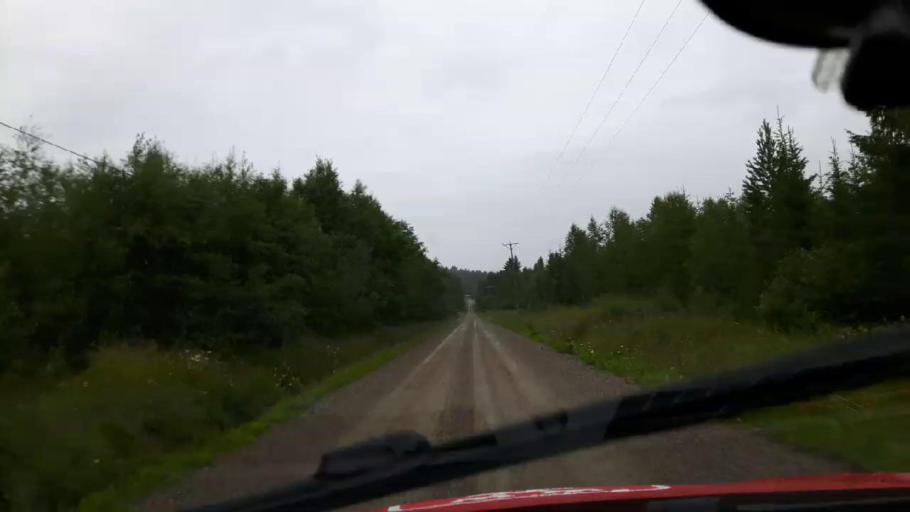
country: SE
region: Jaemtland
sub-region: OEstersunds Kommun
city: Brunflo
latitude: 62.7808
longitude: 14.9768
